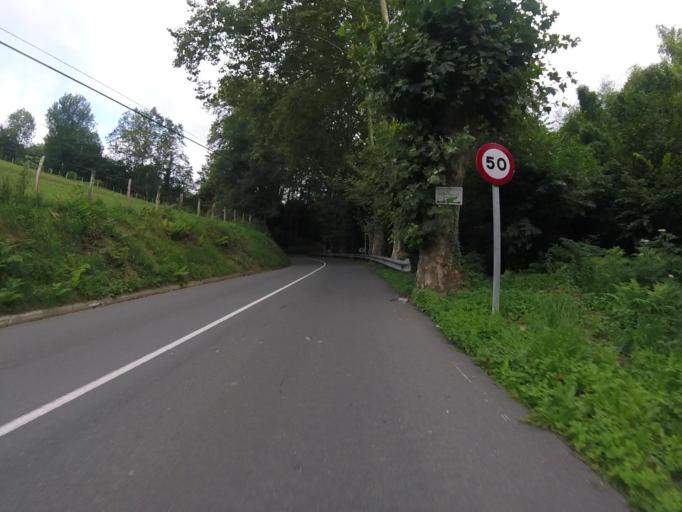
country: ES
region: Basque Country
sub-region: Provincia de Guipuzcoa
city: Irun
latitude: 43.3250
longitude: -1.7892
